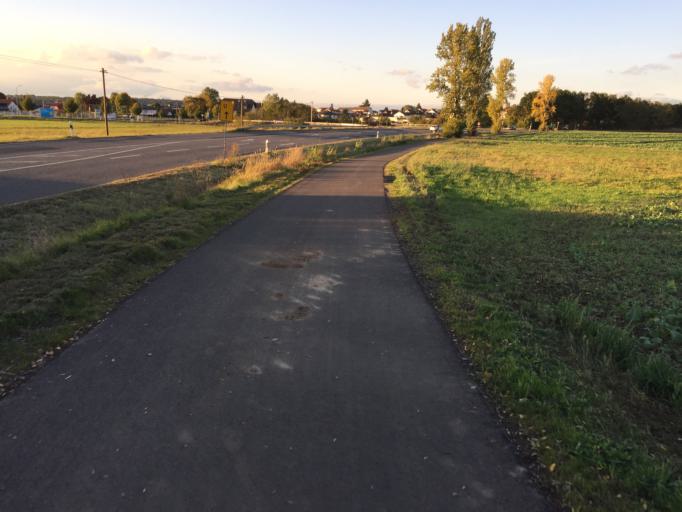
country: DE
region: Hesse
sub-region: Regierungsbezirk Giessen
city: Lich
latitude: 50.5292
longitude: 8.7563
